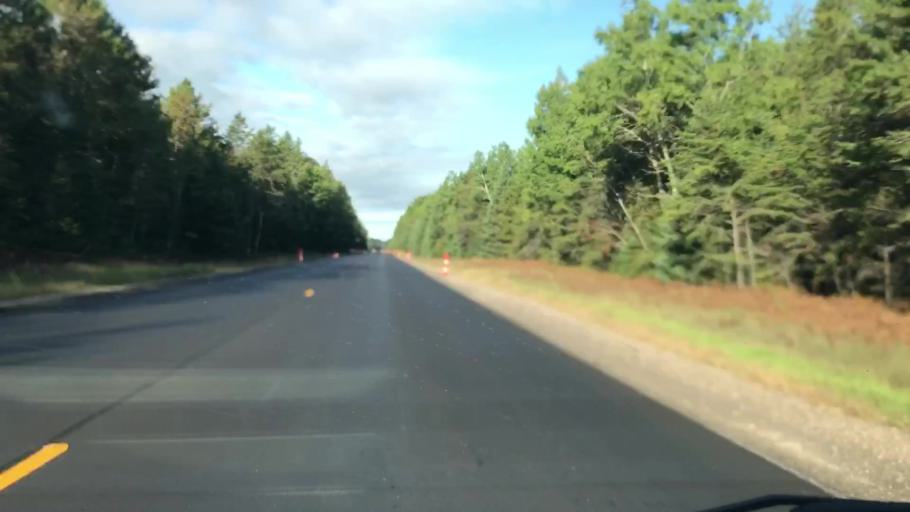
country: US
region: Michigan
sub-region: Mackinac County
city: Saint Ignace
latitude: 46.3459
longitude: -84.9332
